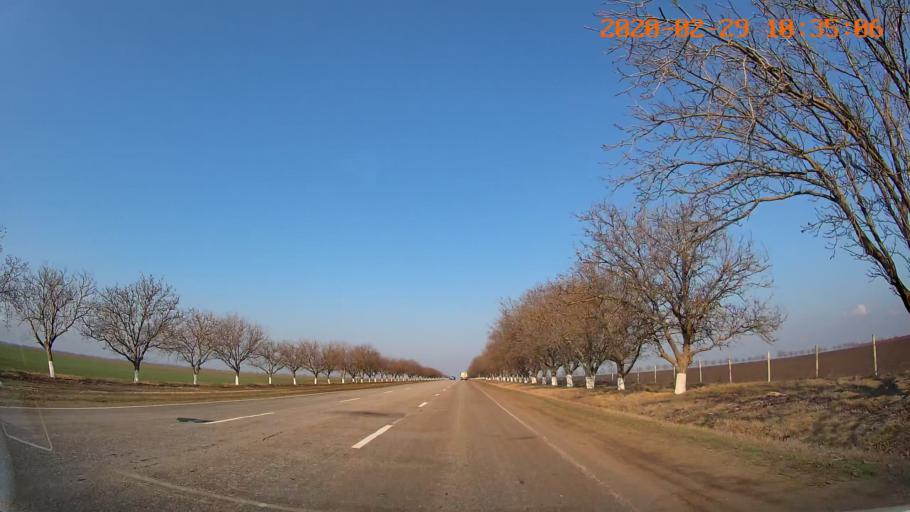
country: MD
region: Anenii Noi
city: Varnita
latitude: 46.9824
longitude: 29.5255
